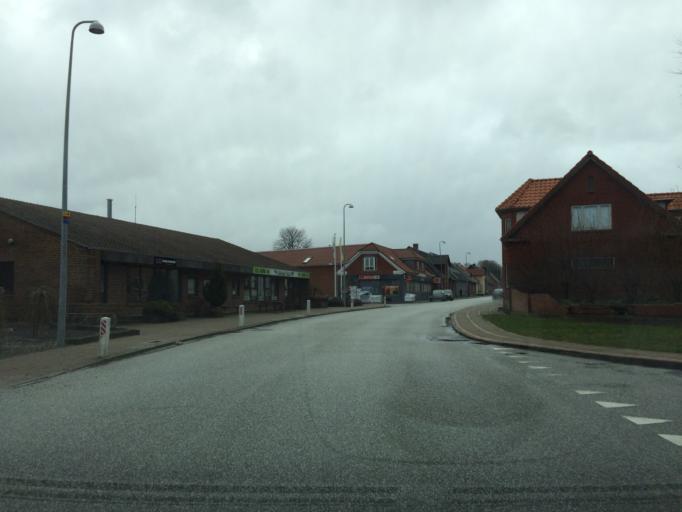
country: DK
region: Central Jutland
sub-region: Ringkobing-Skjern Kommune
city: Videbaek
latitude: 56.2003
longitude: 8.5639
